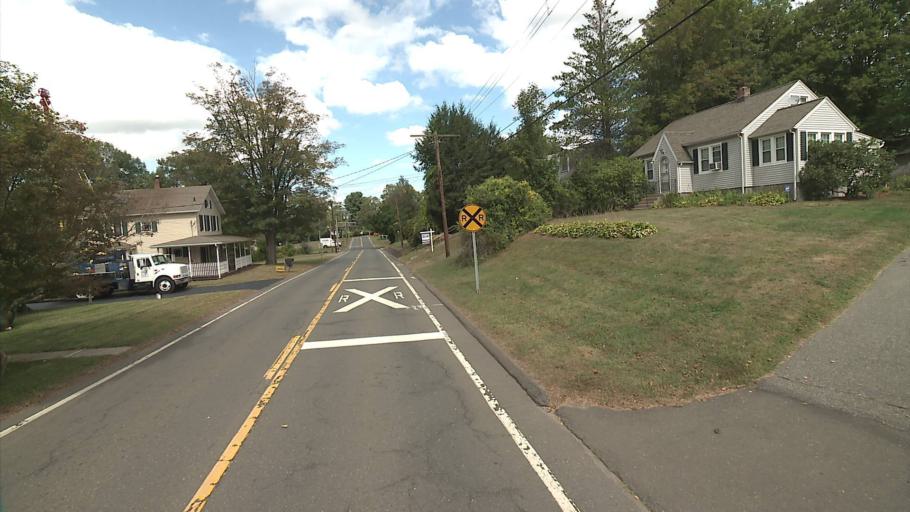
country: US
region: Connecticut
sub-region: Middlesex County
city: Middletown
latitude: 41.5428
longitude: -72.6825
